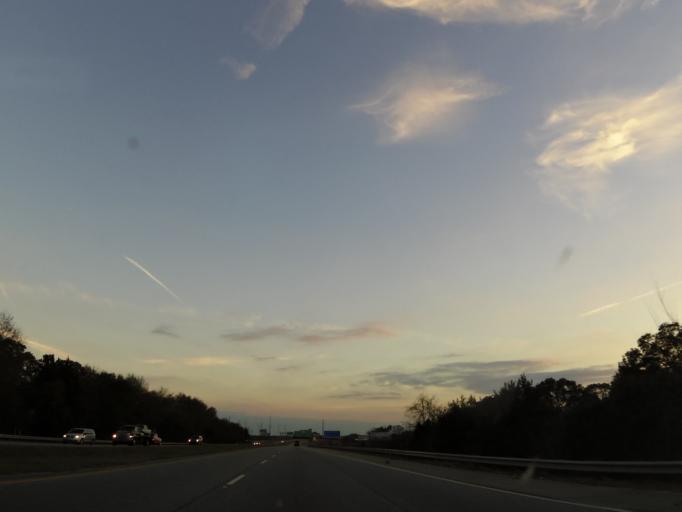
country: US
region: Georgia
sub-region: Dougherty County
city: Albany
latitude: 31.5790
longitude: -84.1118
